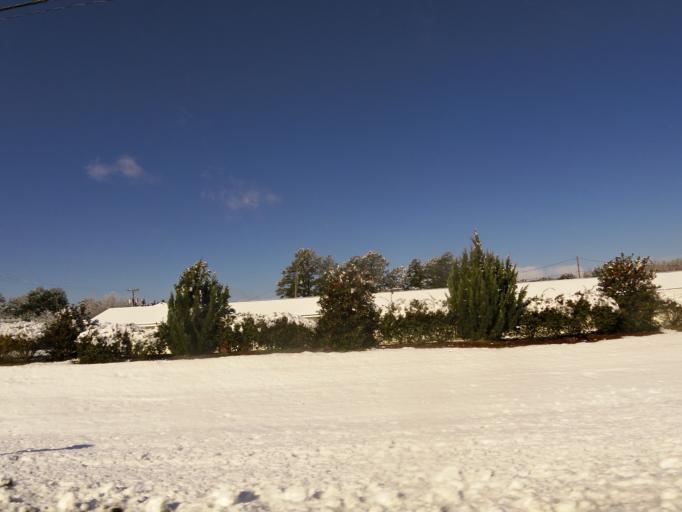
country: US
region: North Carolina
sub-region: Nash County
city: Sharpsburg
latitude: 35.8624
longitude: -77.8327
